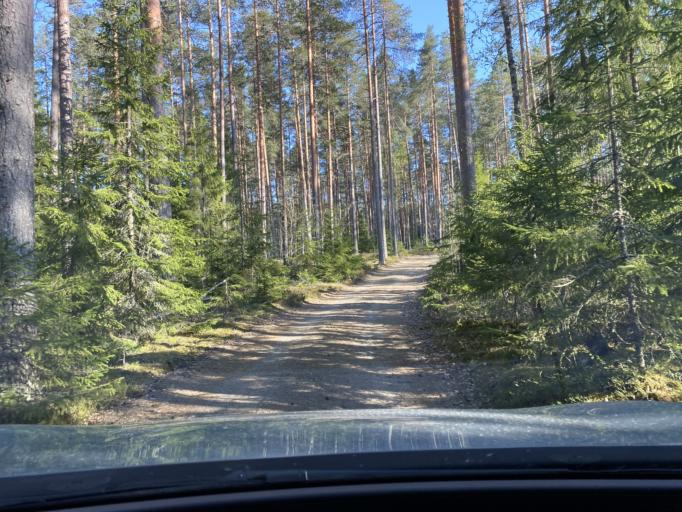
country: FI
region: Pirkanmaa
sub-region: Lounais-Pirkanmaa
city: Punkalaidun
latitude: 61.0143
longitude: 23.2042
